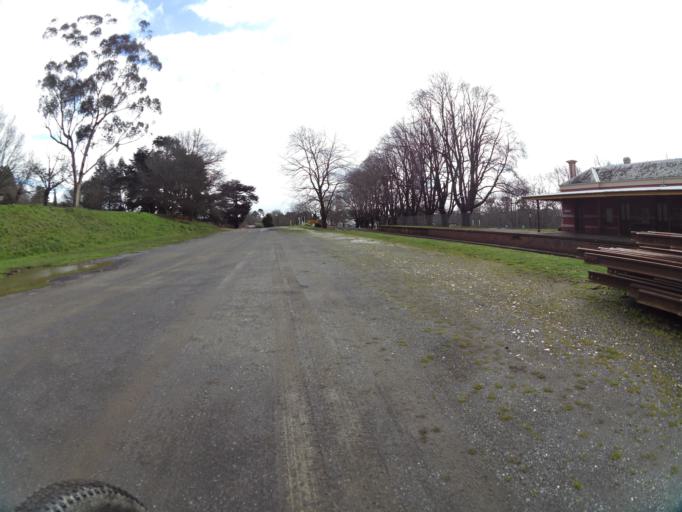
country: AU
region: Victoria
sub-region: Mount Alexander
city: Castlemaine
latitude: -37.3417
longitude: 144.1533
